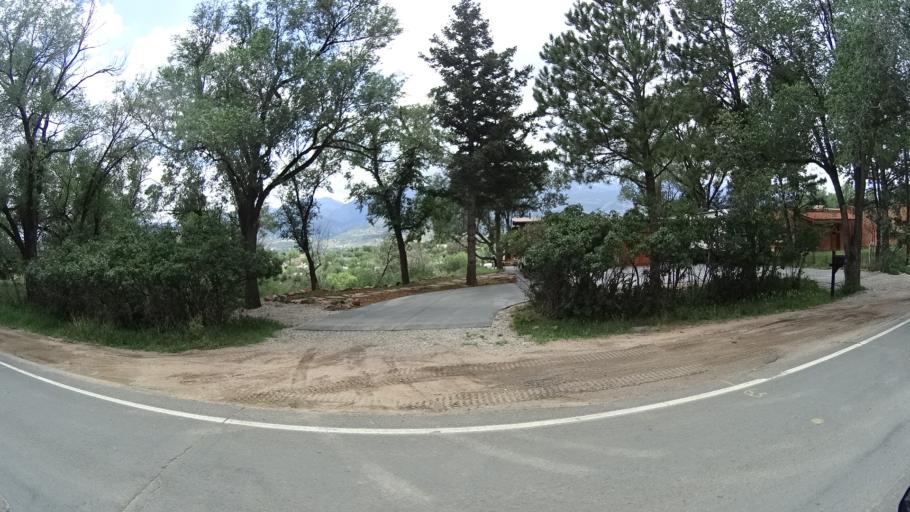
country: US
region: Colorado
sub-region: El Paso County
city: Colorado Springs
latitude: 38.8604
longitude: -104.8489
